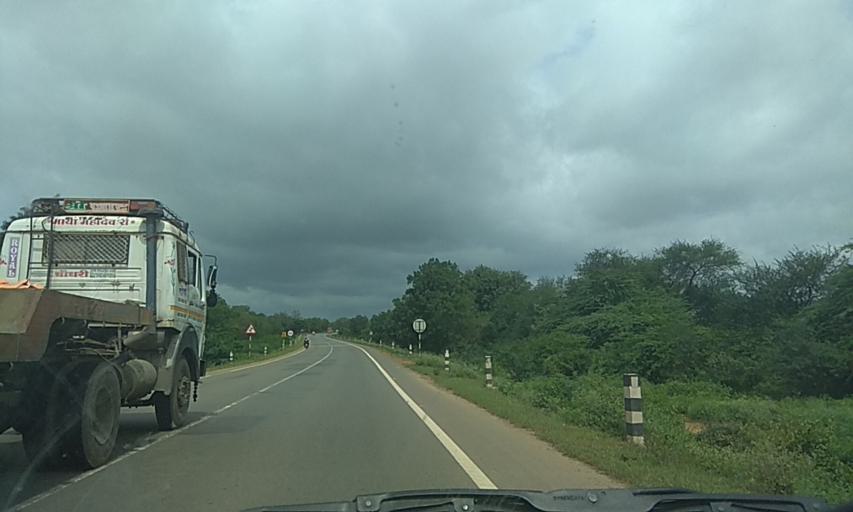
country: IN
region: Karnataka
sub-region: Dharwad
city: Hubli
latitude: 15.3365
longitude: 75.0919
